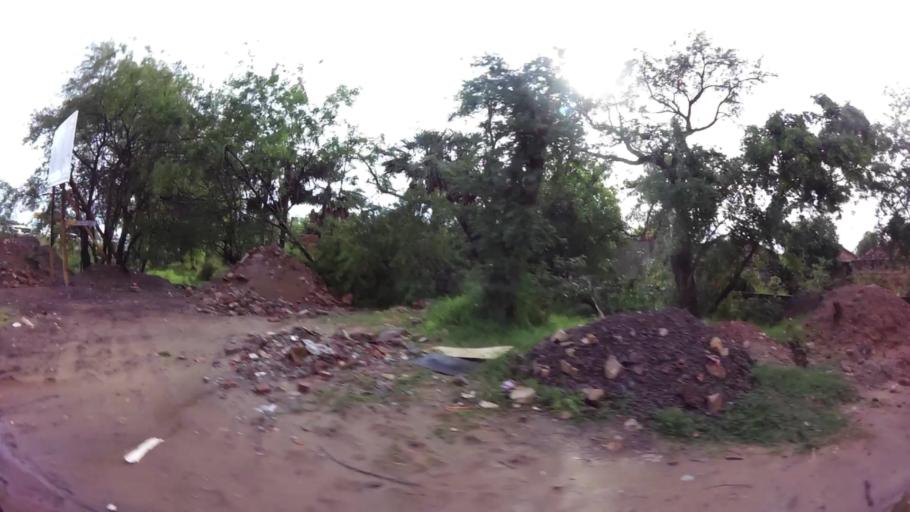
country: PY
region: Central
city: Limpio
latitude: -25.1890
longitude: -57.4973
